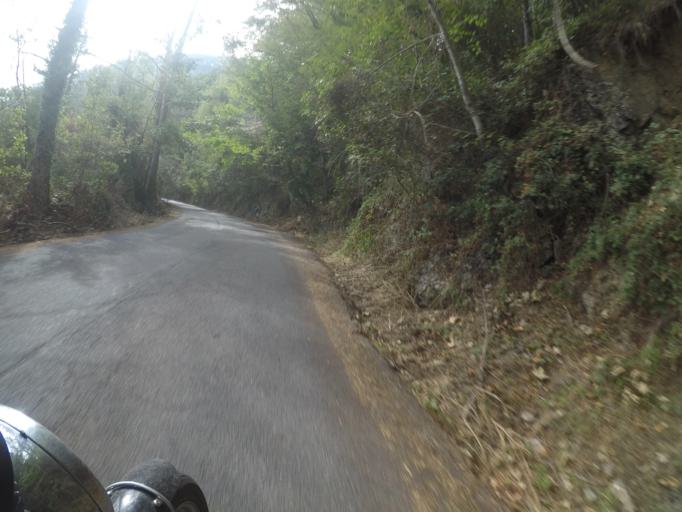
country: IT
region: Tuscany
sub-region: Provincia di Massa-Carrara
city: Fosdinovo
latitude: 44.1237
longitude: 10.0867
